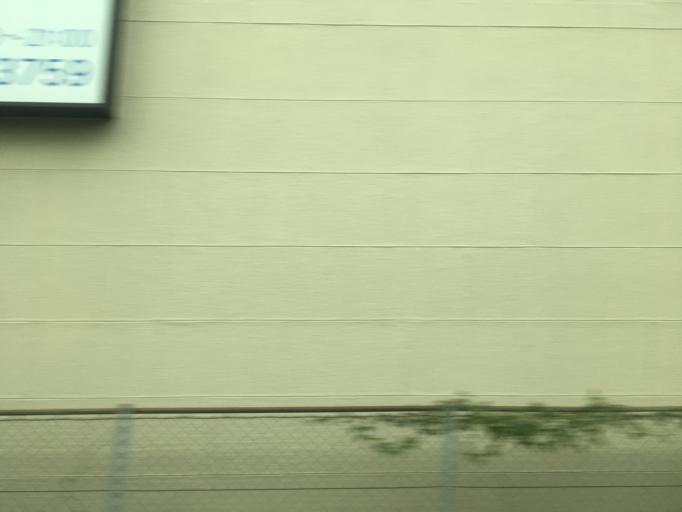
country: JP
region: Saitama
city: Ageoshimo
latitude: 35.9727
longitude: 139.5888
